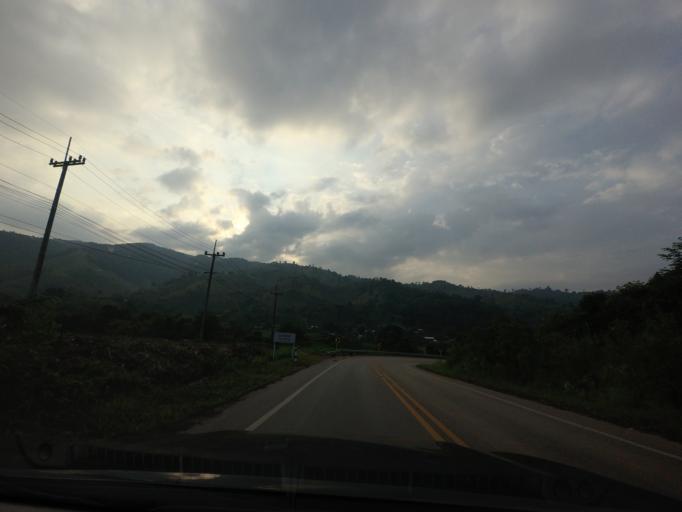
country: TH
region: Loei
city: Na Haeo
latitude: 17.3782
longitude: 101.0440
